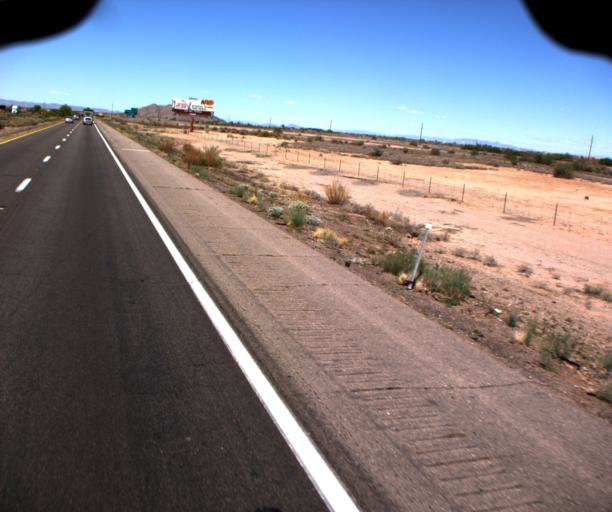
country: US
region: Arizona
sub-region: Pinal County
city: Casa Blanca
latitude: 33.1093
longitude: -111.8351
